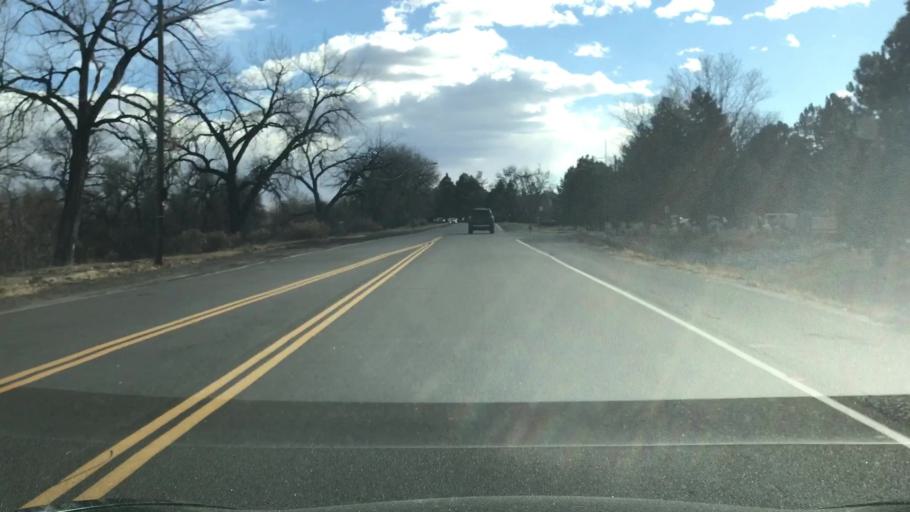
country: US
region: Colorado
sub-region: Arapahoe County
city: Glendale
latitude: 39.6996
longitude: -104.9269
